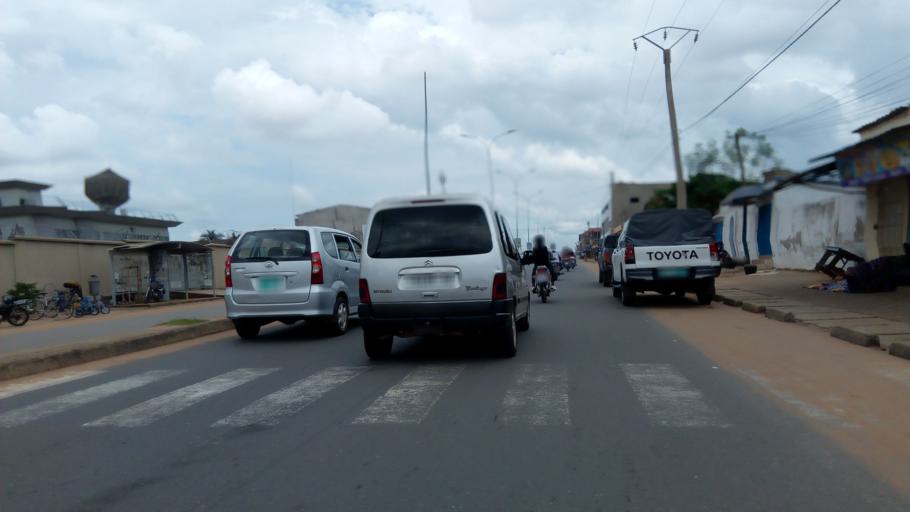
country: TG
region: Maritime
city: Lome
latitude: 6.2124
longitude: 1.1761
